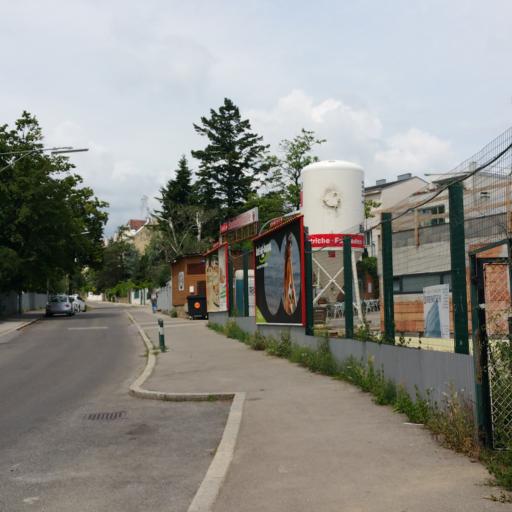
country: AT
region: Vienna
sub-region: Wien Stadt
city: Vienna
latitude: 48.2151
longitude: 16.3037
